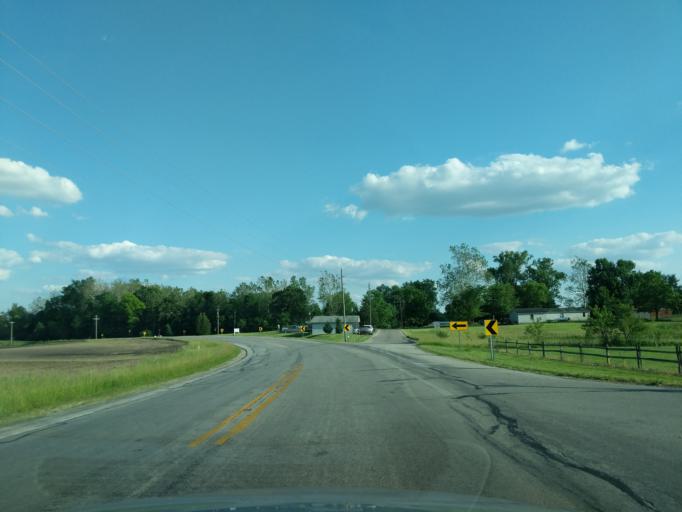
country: US
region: Indiana
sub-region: Whitley County
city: Tri-Lakes
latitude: 41.2847
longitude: -85.5008
